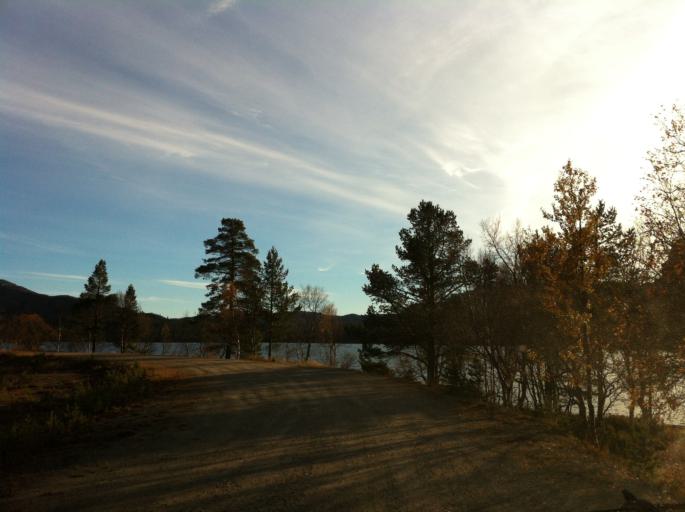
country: NO
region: Hedmark
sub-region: Engerdal
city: Engerdal
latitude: 62.1095
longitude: 12.0193
